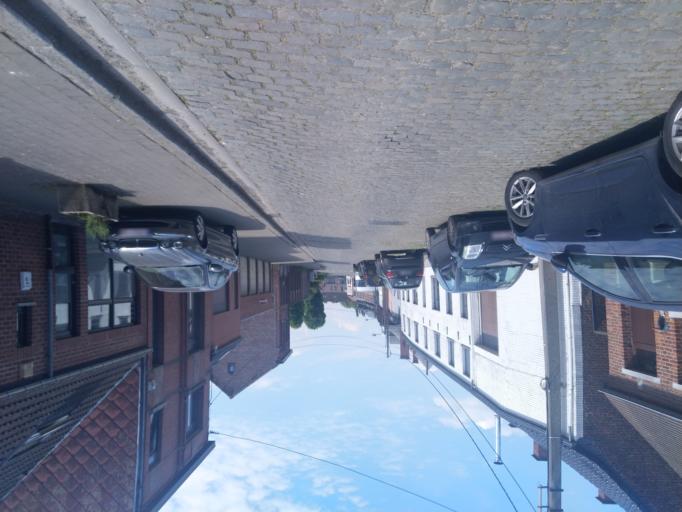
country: BE
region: Wallonia
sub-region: Province du Hainaut
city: Mons
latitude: 50.4390
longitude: 4.0049
